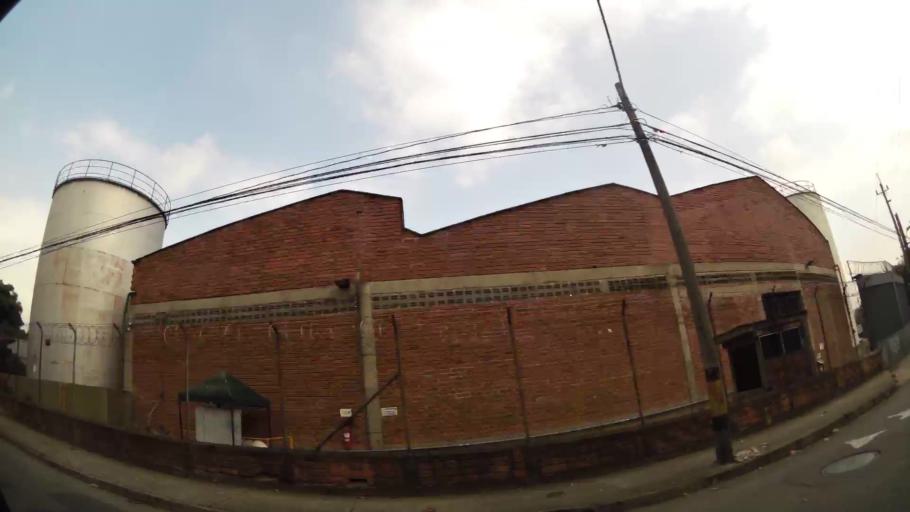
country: CO
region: Antioquia
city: Itagui
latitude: 6.2146
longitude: -75.5787
